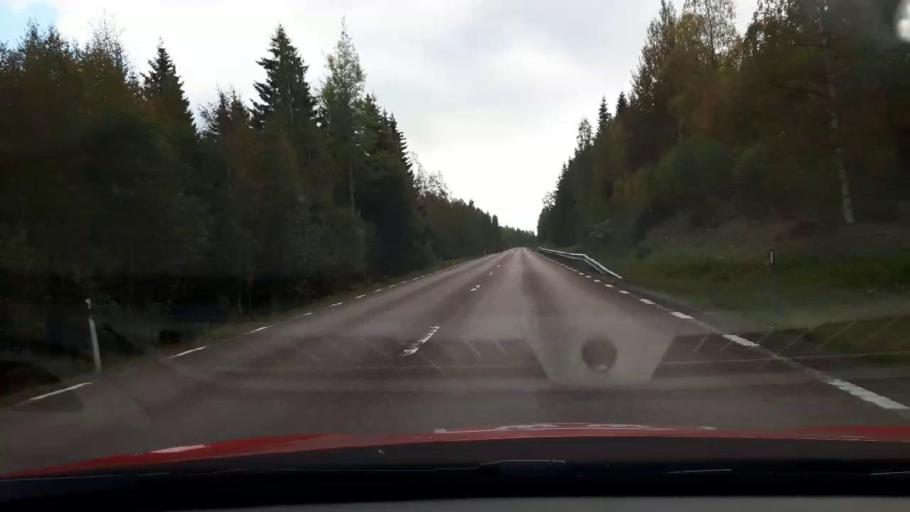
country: SE
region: Gaevleborg
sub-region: Bollnas Kommun
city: Arbra
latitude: 61.5609
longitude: 16.3394
